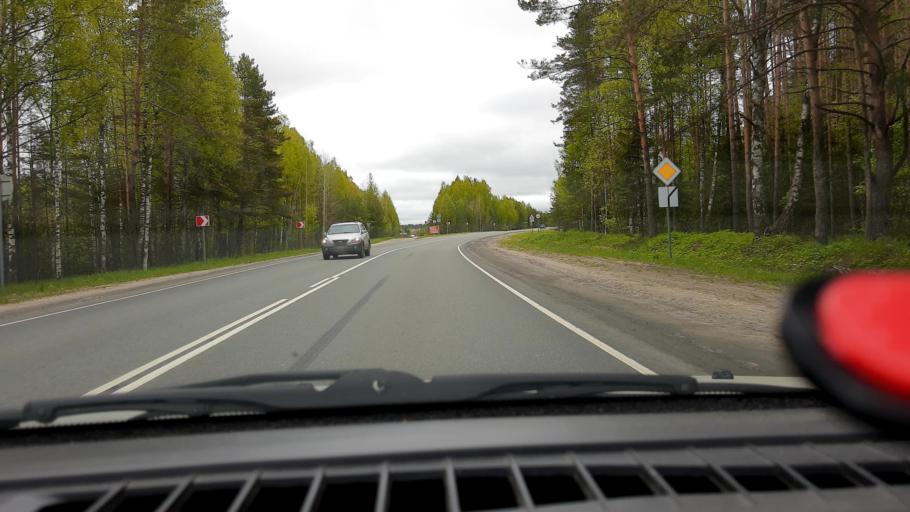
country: RU
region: Nizjnij Novgorod
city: Semenov
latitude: 56.7261
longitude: 44.2880
